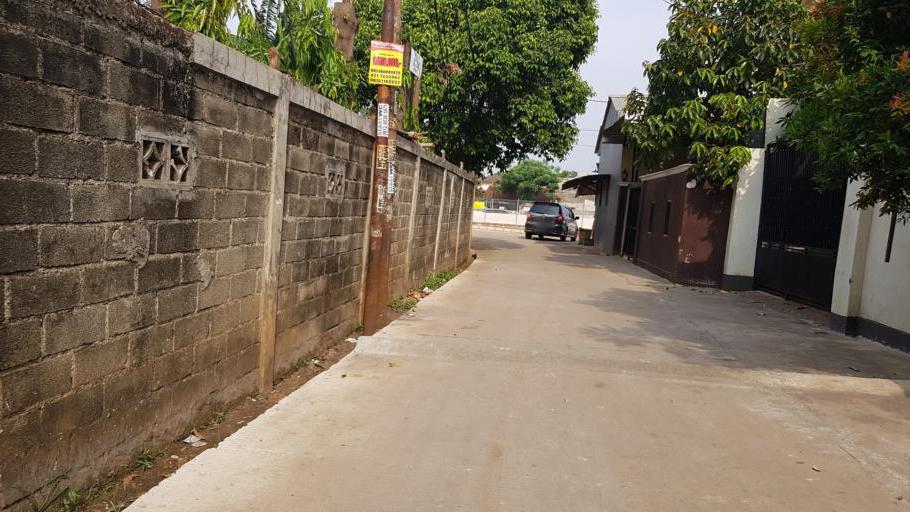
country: ID
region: West Java
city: Pamulang
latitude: -6.3227
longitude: 106.8024
